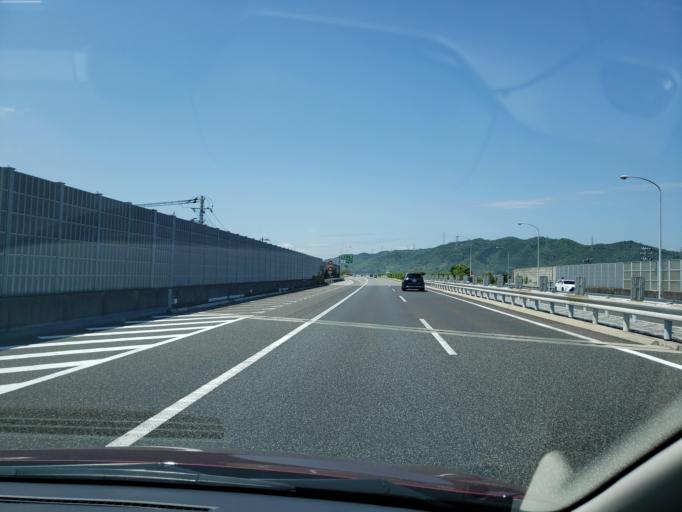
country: JP
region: Hyogo
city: Fukura
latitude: 34.3135
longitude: 134.7550
